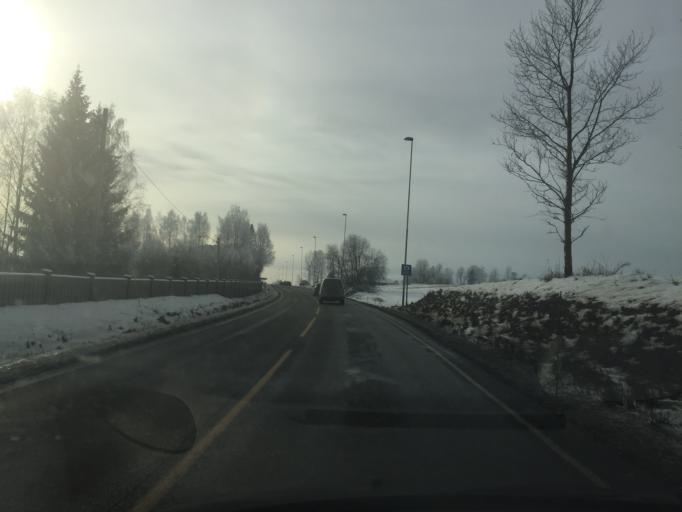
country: NO
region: Hedmark
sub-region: Loten
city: Loten
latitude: 60.8335
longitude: 11.3522
